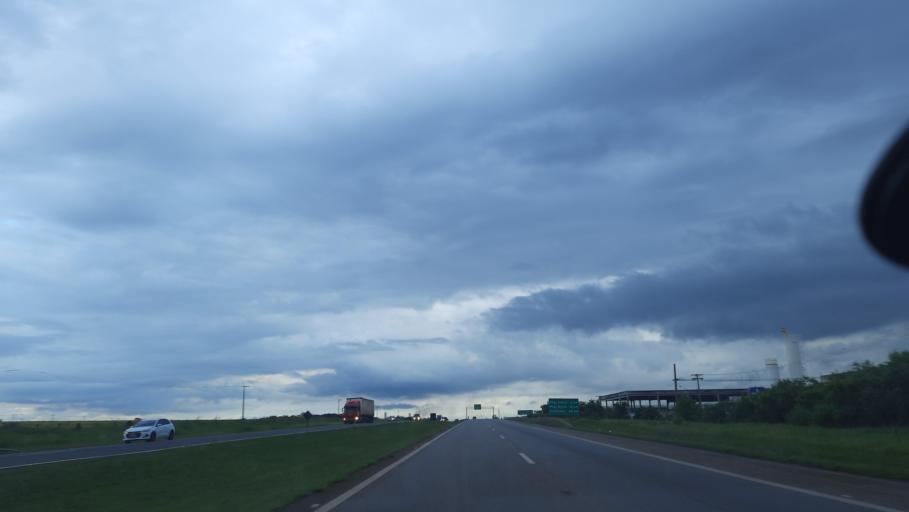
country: BR
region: Sao Paulo
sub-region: Moji-Guacu
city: Mogi-Gaucu
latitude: -22.2973
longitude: -46.9689
